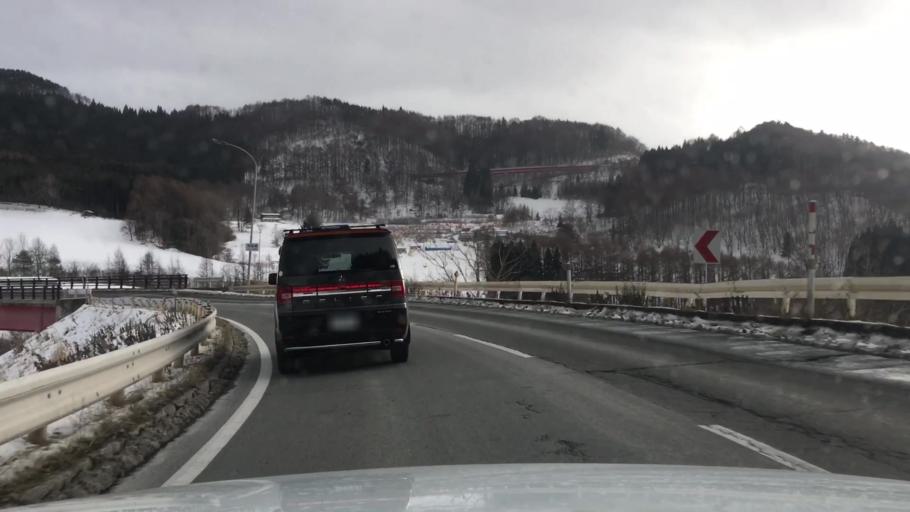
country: JP
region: Iwate
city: Morioka-shi
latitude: 39.6714
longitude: 141.3276
